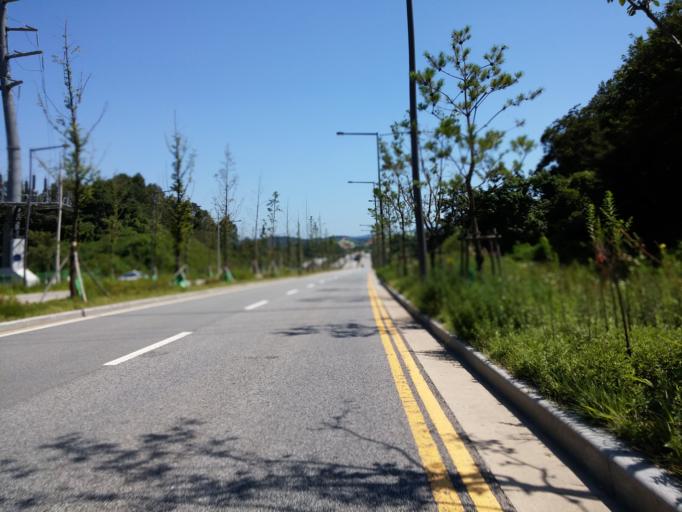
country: KR
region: Daejeon
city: Songgang-dong
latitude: 36.5333
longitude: 127.2730
